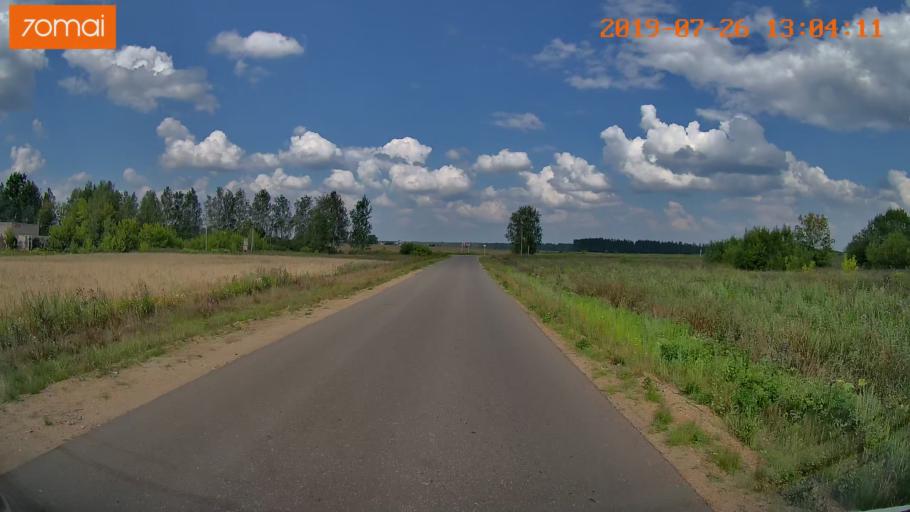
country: RU
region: Ivanovo
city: Bogorodskoye
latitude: 57.0537
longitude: 41.0219
